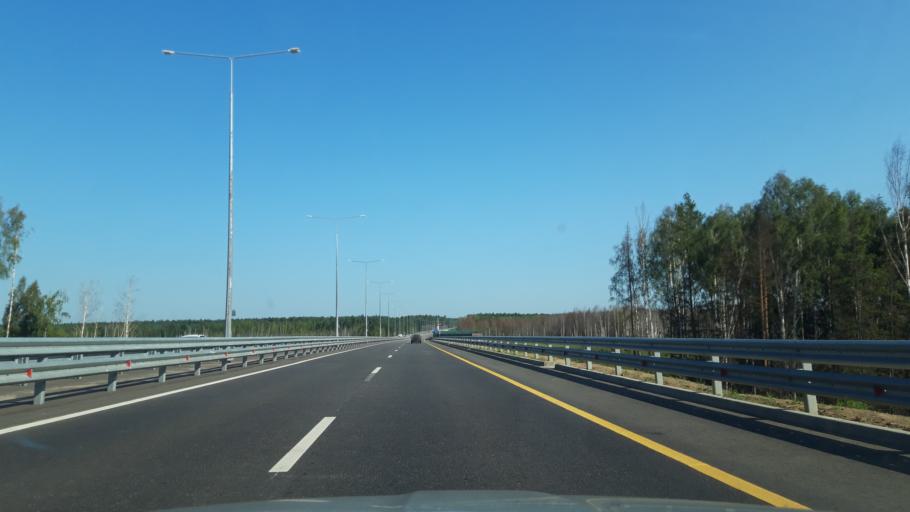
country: RU
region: Moskovskaya
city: Reshetnikovo
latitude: 56.4274
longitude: 36.5485
